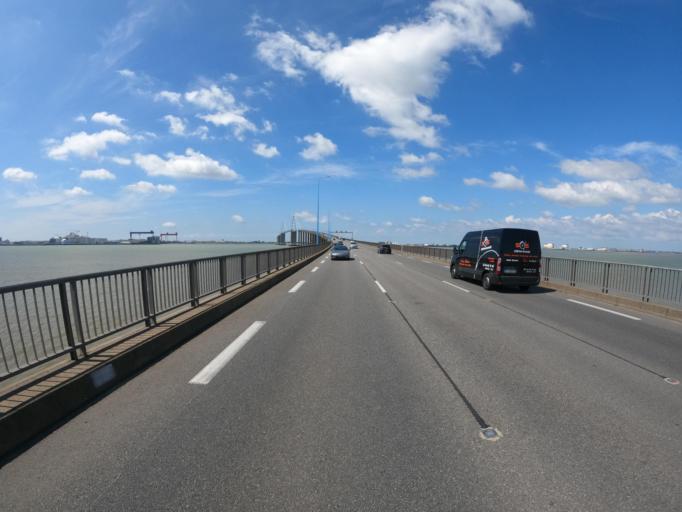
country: FR
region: Pays de la Loire
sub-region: Departement de la Loire-Atlantique
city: Saint-Brevin-les-Pins
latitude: 47.2735
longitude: -2.1634
